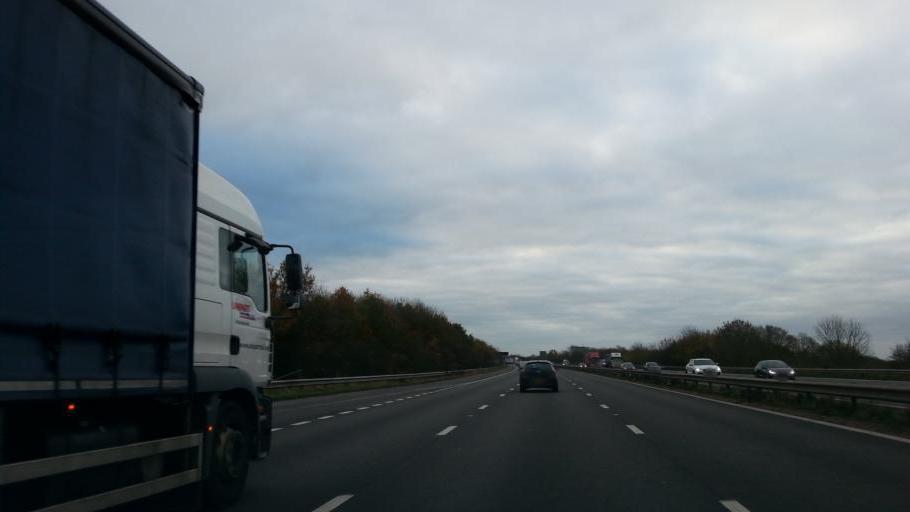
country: GB
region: England
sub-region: Leicestershire
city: Lutterworth
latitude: 52.4313
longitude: -1.1929
